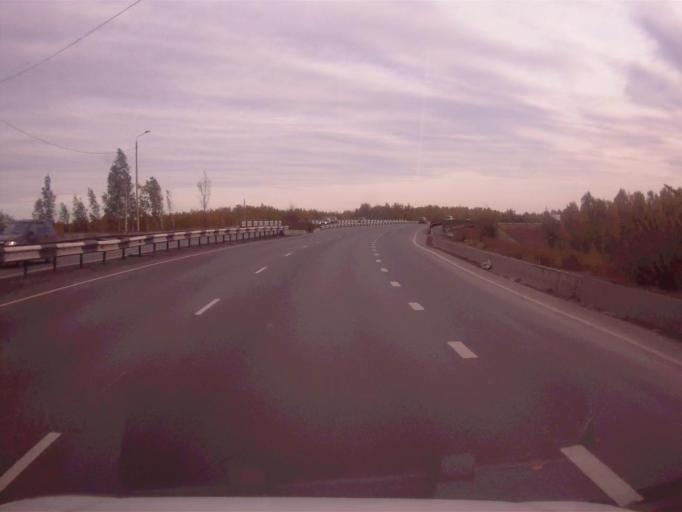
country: RU
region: Chelyabinsk
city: Novosineglazovskiy
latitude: 55.0404
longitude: 61.4381
